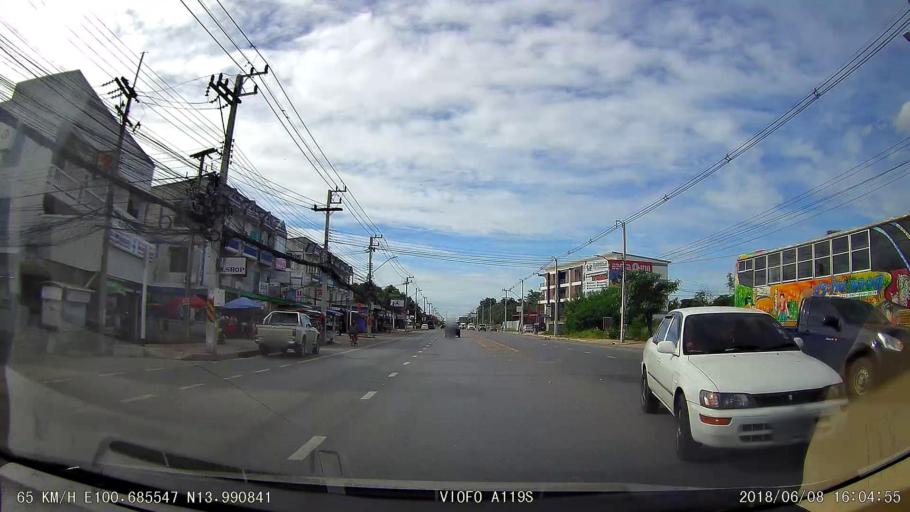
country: TH
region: Pathum Thani
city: Thanyaburi
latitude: 13.9911
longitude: 100.6855
